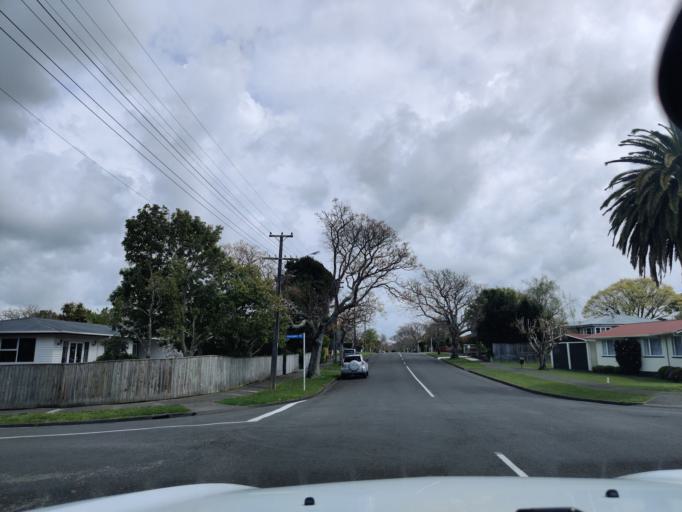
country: NZ
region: Manawatu-Wanganui
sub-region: Palmerston North City
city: Palmerston North
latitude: -40.3794
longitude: 175.5924
